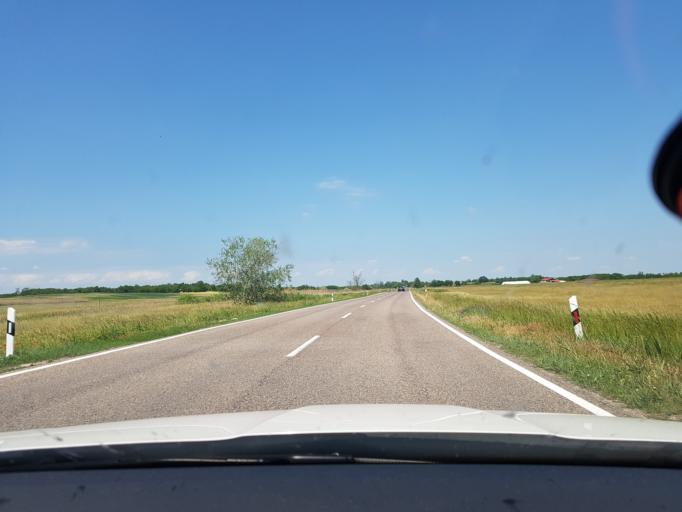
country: HU
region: Hajdu-Bihar
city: Egyek
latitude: 47.5805
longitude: 20.8542
